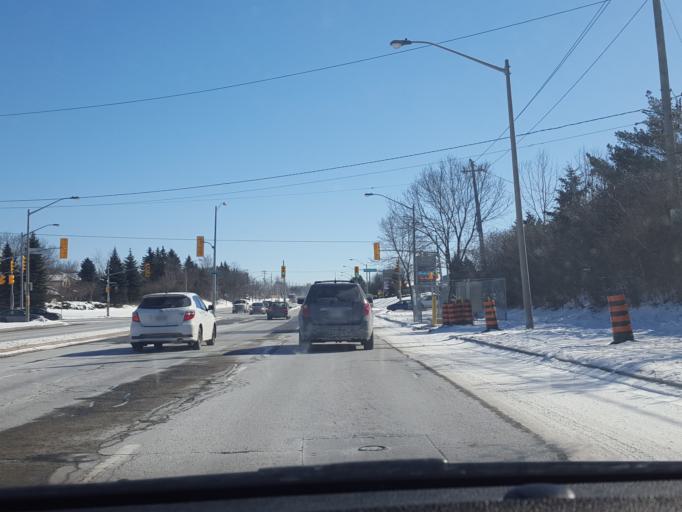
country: CA
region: Ontario
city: Waterloo
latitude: 43.4445
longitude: -80.5463
